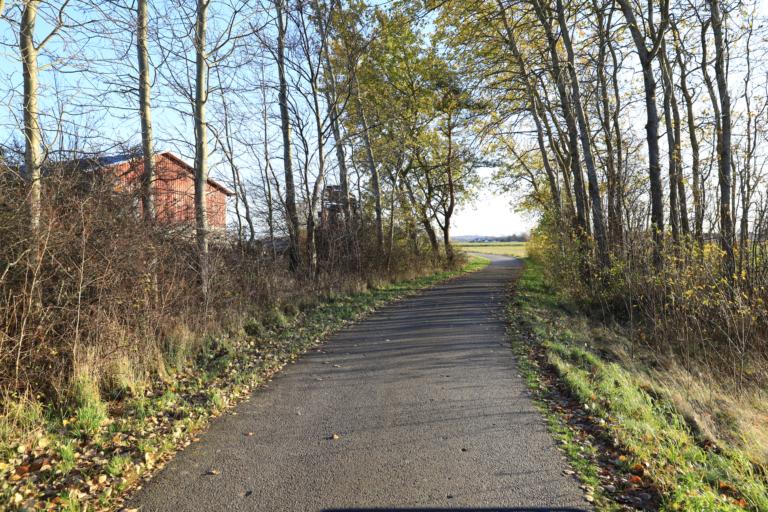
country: SE
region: Halland
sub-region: Varbergs Kommun
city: Varberg
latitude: 57.1549
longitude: 12.2410
